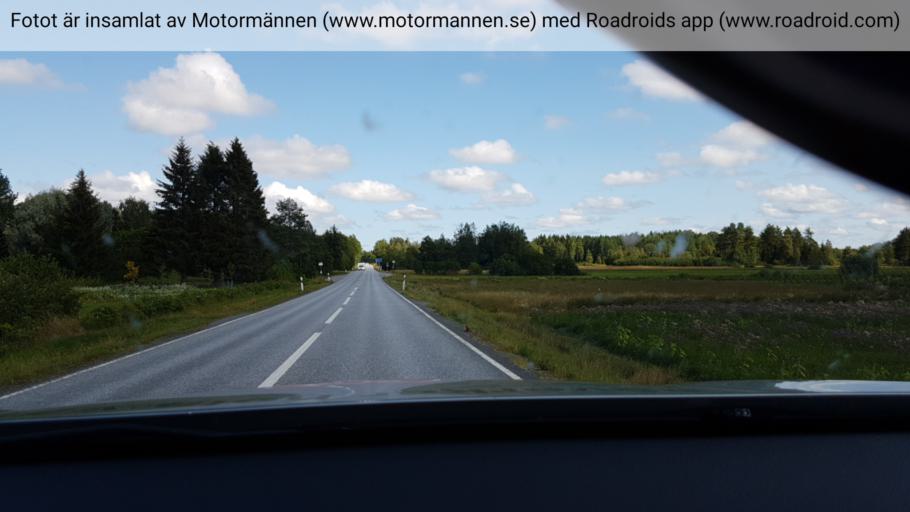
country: SE
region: Stockholm
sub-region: Norrtalje Kommun
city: Hallstavik
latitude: 59.9454
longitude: 18.7555
